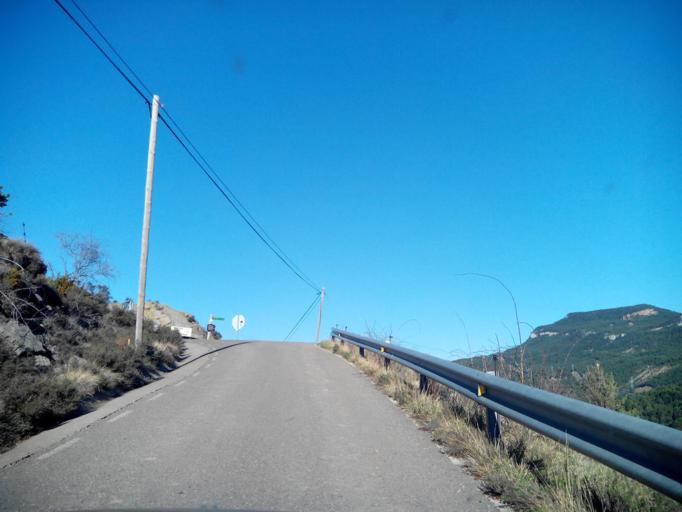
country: ES
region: Catalonia
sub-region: Provincia de Barcelona
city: Saldes
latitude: 42.2235
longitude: 1.7253
